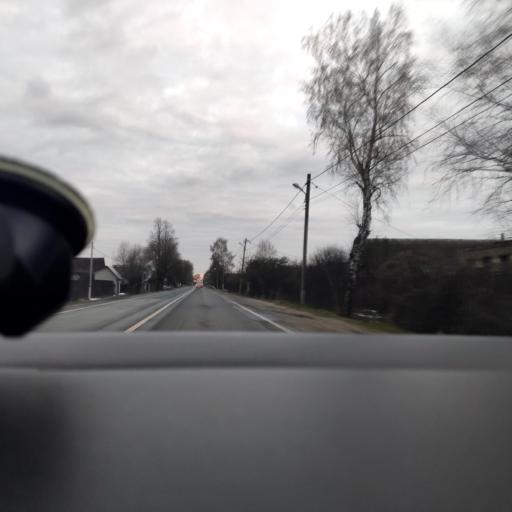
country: RU
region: Moskovskaya
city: Imeni Tsyurupy
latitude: 55.5759
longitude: 38.5933
